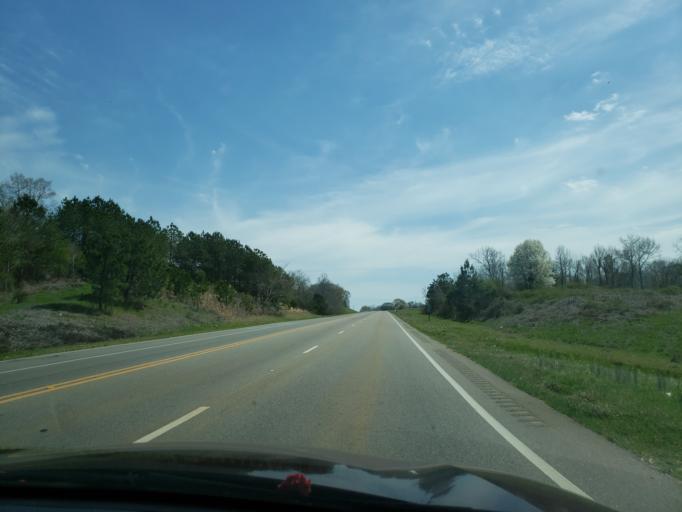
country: US
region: Alabama
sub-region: Autauga County
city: Prattville
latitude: 32.4320
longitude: -86.5580
